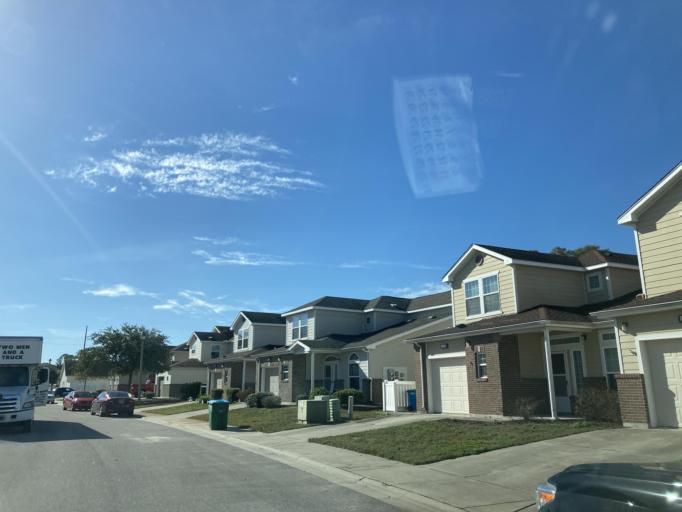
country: US
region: Mississippi
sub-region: Harrison County
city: D'Iberville
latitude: 30.4056
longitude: -88.9493
